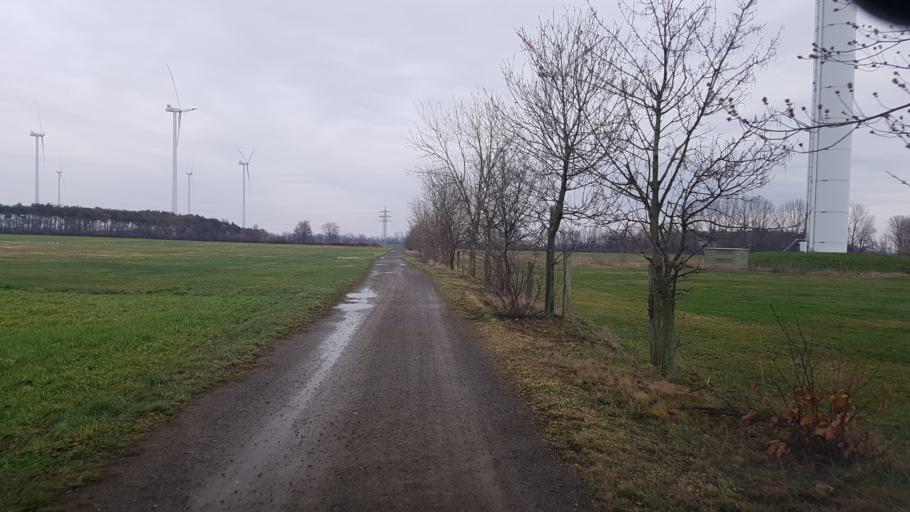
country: DE
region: Brandenburg
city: Bad Liebenwerda
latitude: 51.5212
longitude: 13.3190
